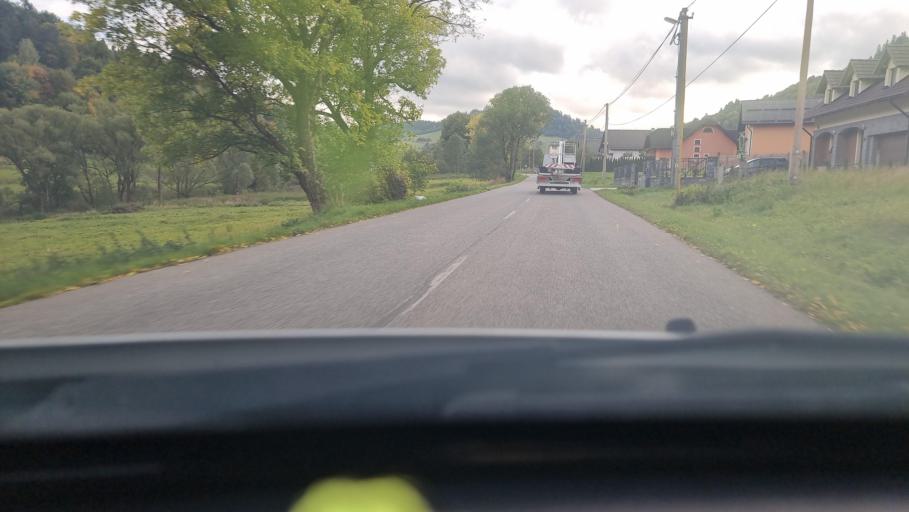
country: PL
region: Lesser Poland Voivodeship
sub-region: Powiat nowotarski
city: Szczawnica
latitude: 49.3396
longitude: 20.4382
